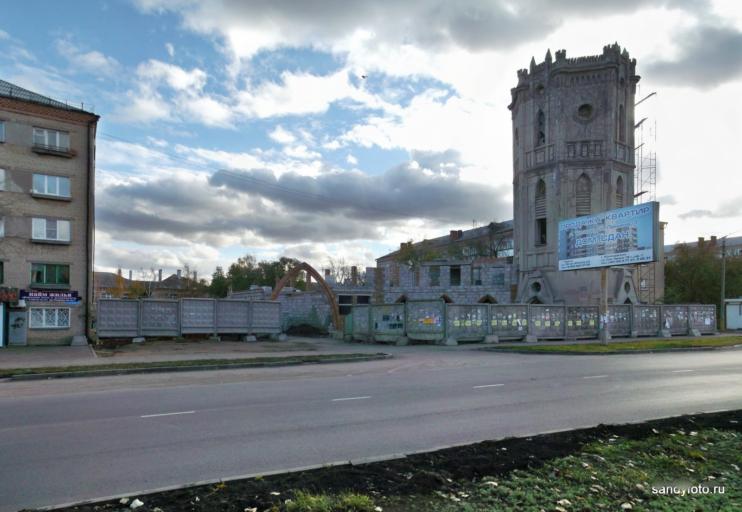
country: RU
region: Chelyabinsk
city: Troitsk
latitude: 54.0813
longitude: 61.5337
